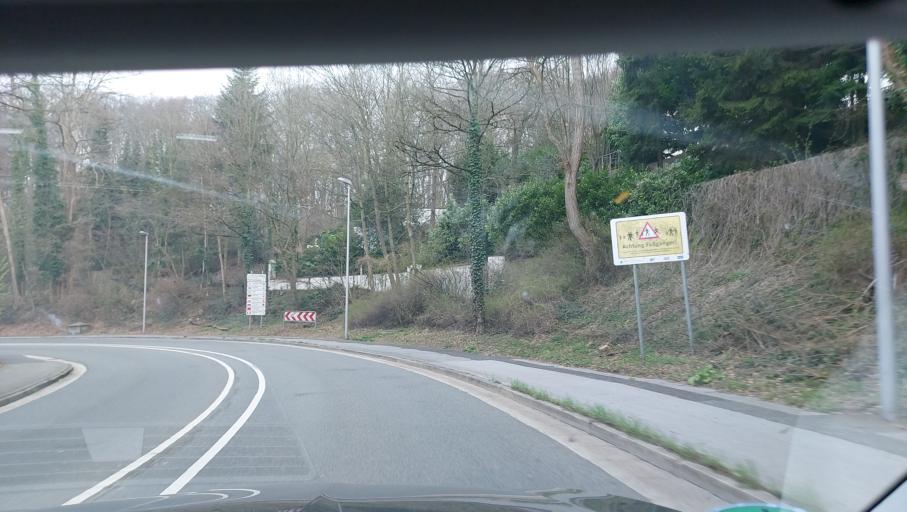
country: DE
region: North Rhine-Westphalia
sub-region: Regierungsbezirk Dusseldorf
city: Ratingen
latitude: 51.2471
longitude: 6.8601
